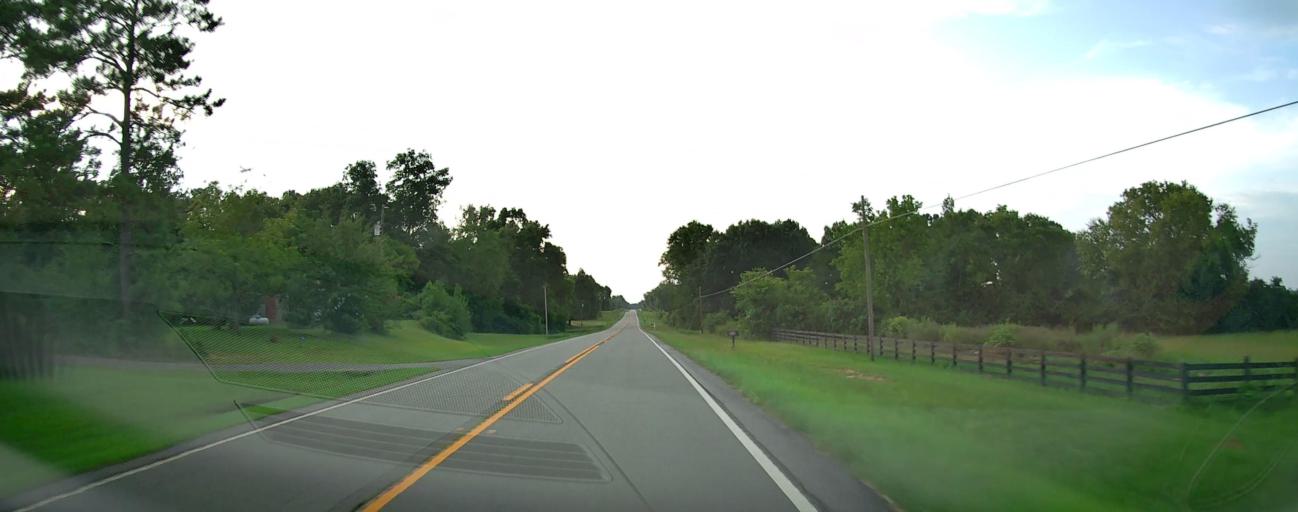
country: US
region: Georgia
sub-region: Taylor County
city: Reynolds
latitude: 32.5997
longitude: -84.0938
